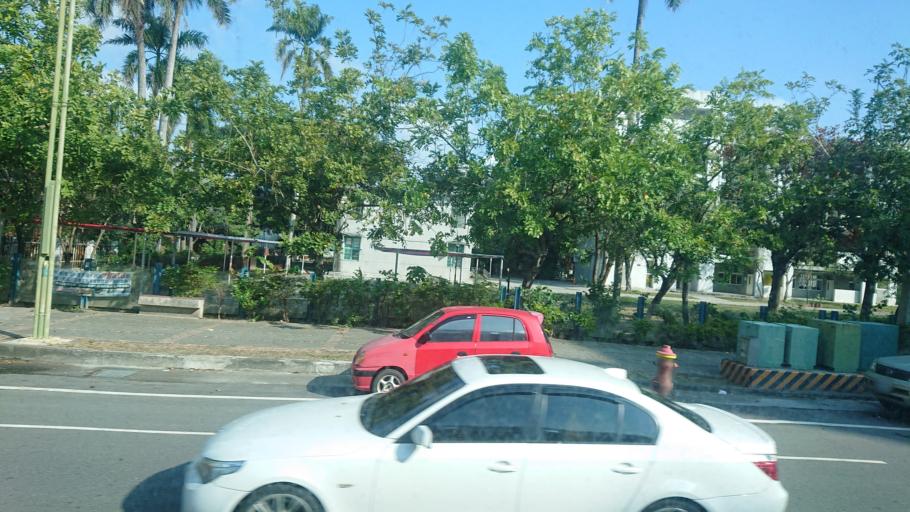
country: TW
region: Taiwan
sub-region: Chiayi
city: Taibao
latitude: 23.4670
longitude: 120.2499
